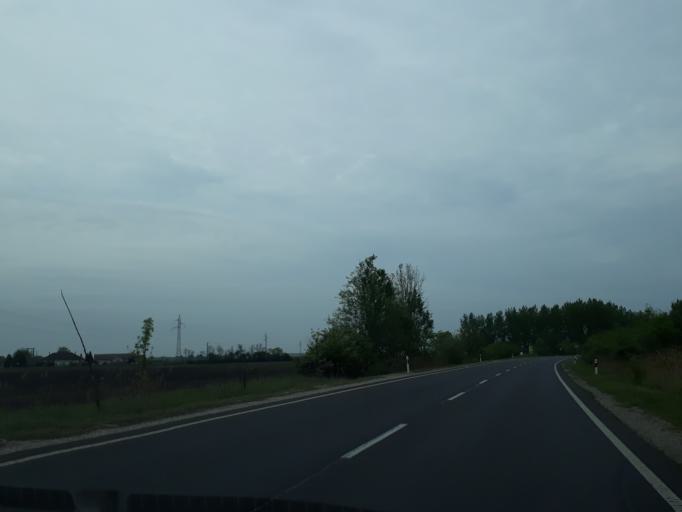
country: HU
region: Szabolcs-Szatmar-Bereg
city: Nyirbogdany
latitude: 48.0625
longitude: 21.9280
